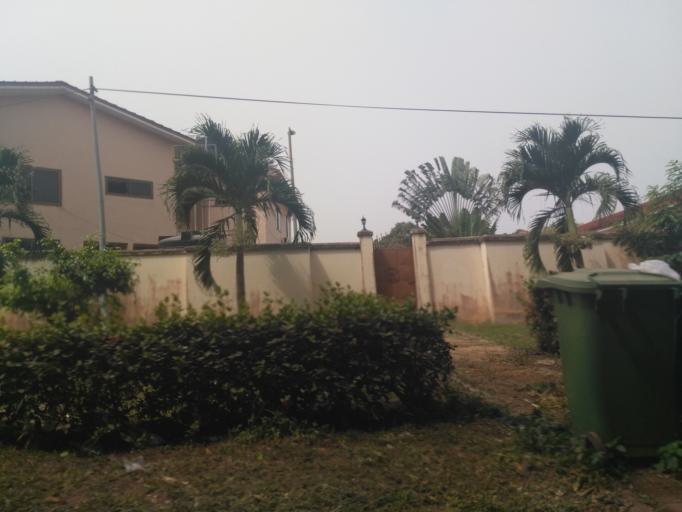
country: GH
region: Ashanti
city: Kumasi
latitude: 6.6858
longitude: -1.6338
